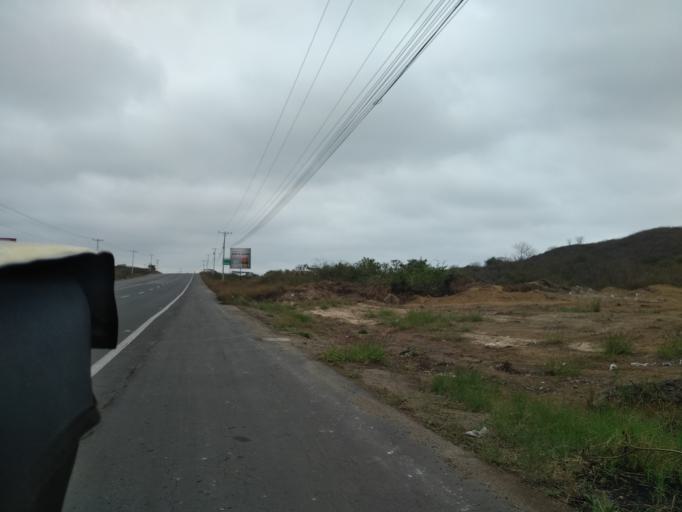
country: EC
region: Santa Elena
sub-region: Canton Santa Elena
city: Santa Elena
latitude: -2.2059
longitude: -80.8593
